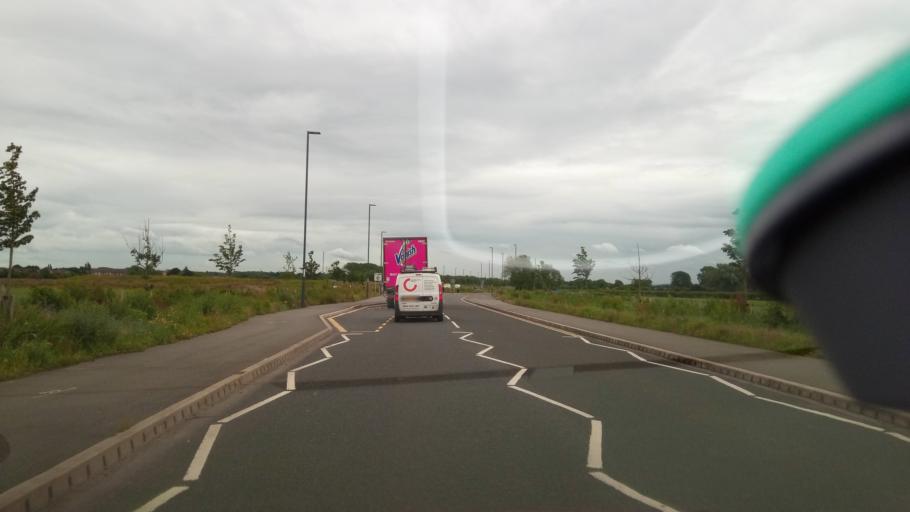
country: GB
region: England
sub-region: Derby
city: Derby
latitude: 52.8753
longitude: -1.4641
